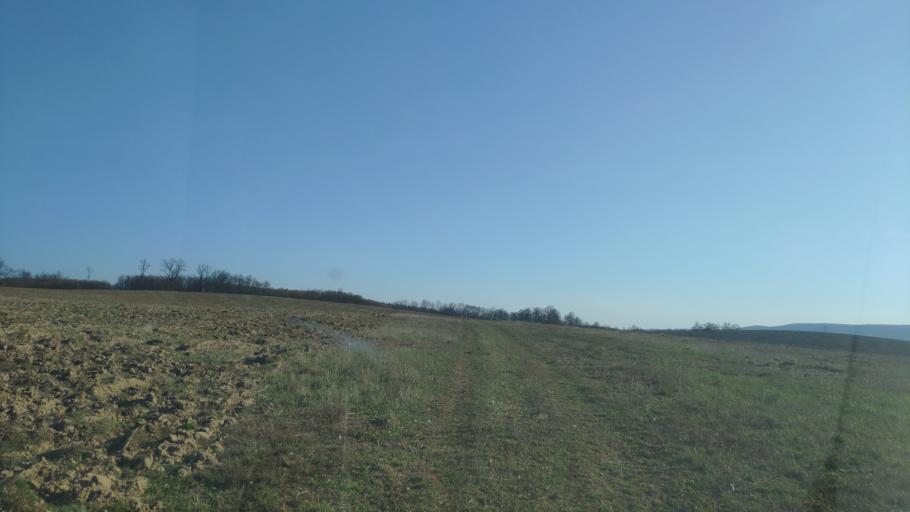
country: SK
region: Banskobystricky
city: Revuca
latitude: 48.5435
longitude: 20.2568
